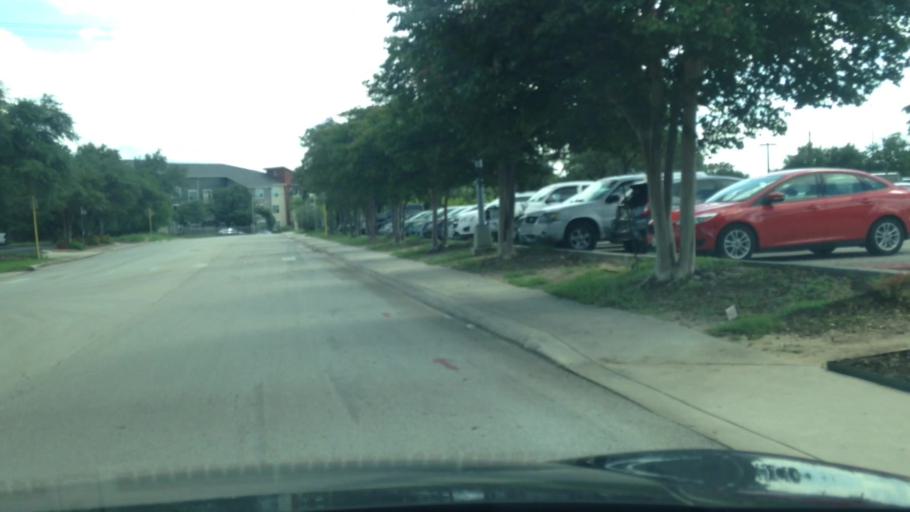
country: US
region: Texas
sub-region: Bexar County
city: Shavano Park
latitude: 29.5449
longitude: -98.5865
